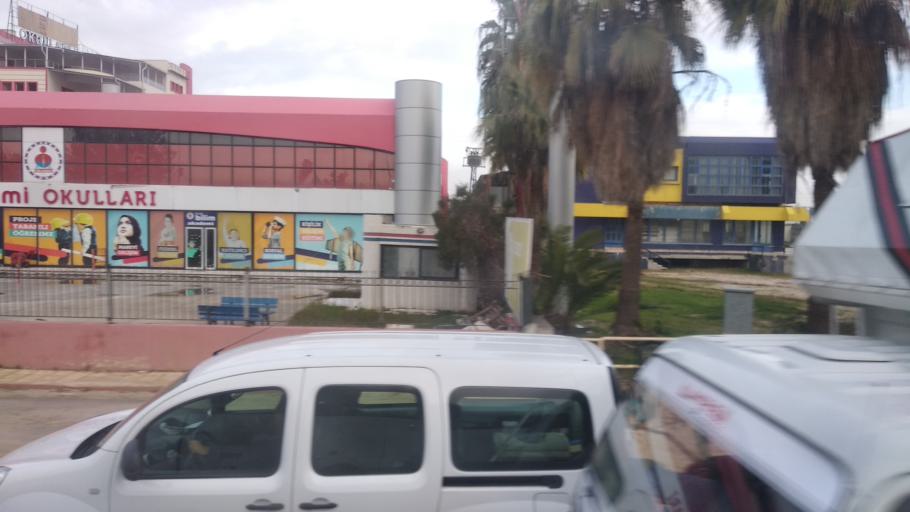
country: TR
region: Adana
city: Seyhan
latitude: 36.9950
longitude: 35.2140
